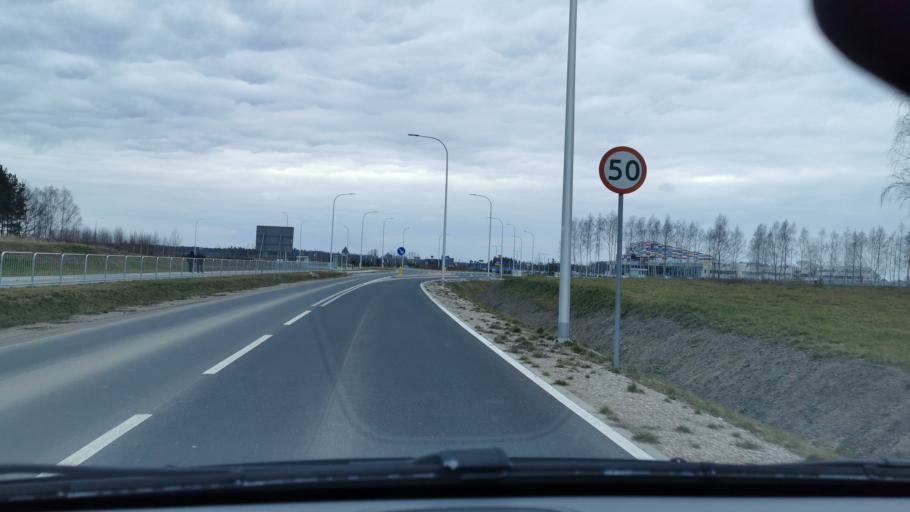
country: PL
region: Masovian Voivodeship
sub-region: Powiat zyrardowski
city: Mszczonow
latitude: 51.9922
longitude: 20.4644
